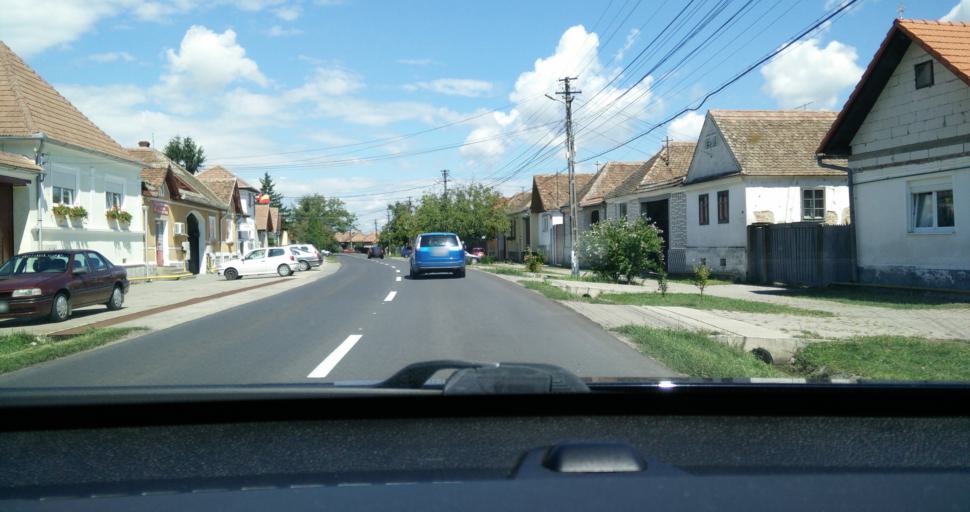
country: RO
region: Alba
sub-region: Municipiul Sebes
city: Petresti
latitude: 45.9226
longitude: 23.5622
